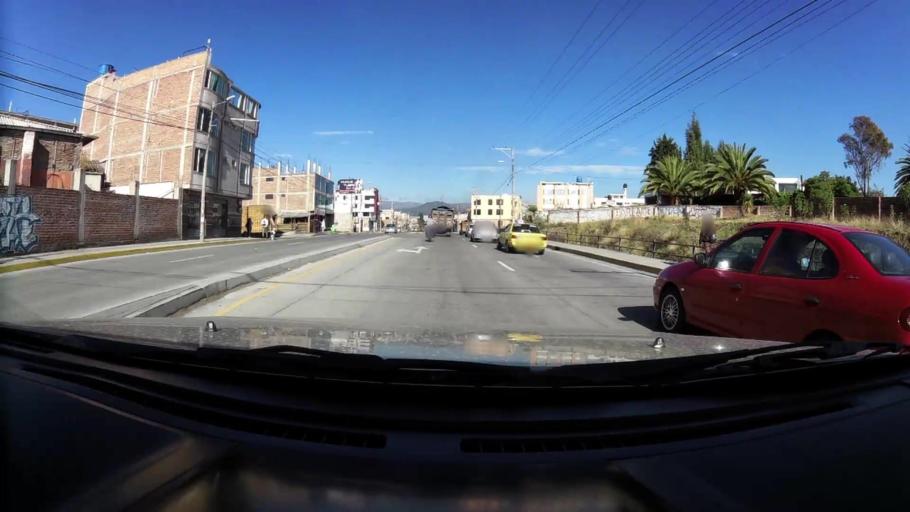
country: EC
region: Chimborazo
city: Riobamba
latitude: -1.6627
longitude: -78.6725
